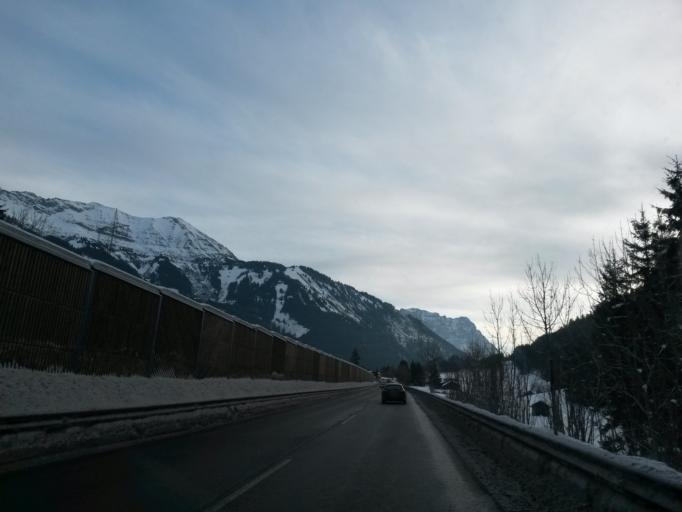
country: AT
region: Tyrol
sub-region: Politischer Bezirk Reutte
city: Bichlbach
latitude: 47.4184
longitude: 10.8227
